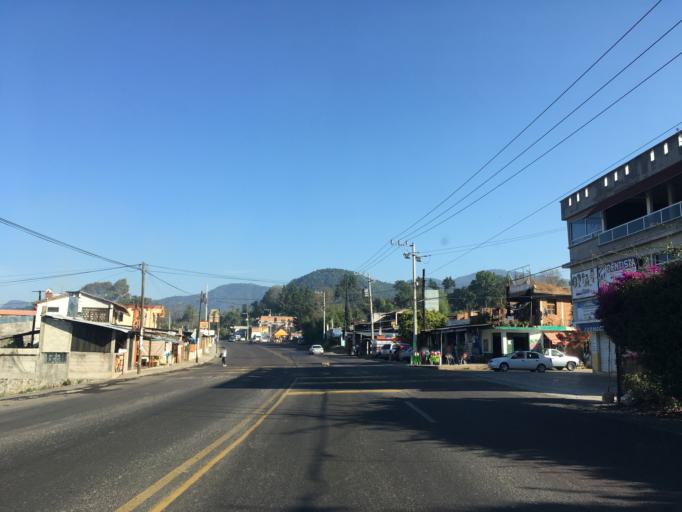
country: MX
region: Michoacan
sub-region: Zitacuaro
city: Valle Verde
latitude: 19.4640
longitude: -100.3435
